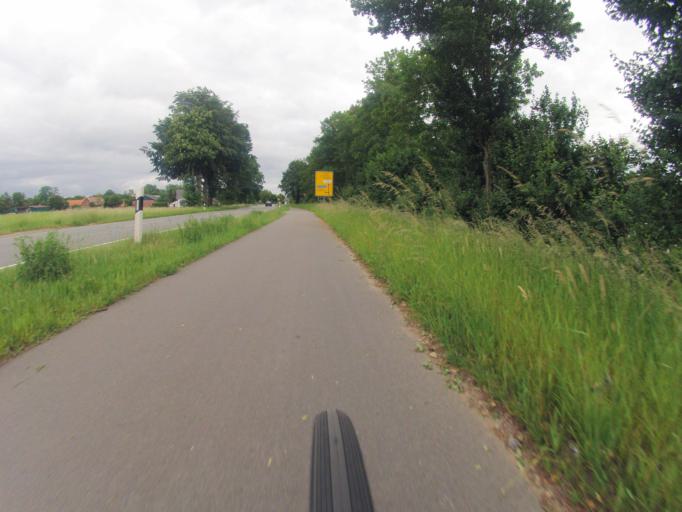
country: DE
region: North Rhine-Westphalia
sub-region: Regierungsbezirk Munster
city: Birgte
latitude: 52.2348
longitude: 7.6912
